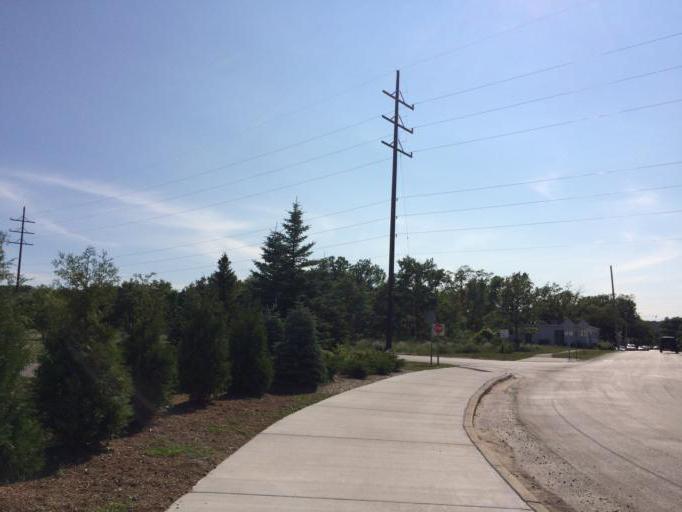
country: US
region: Michigan
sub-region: Grand Traverse County
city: Traverse City
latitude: 44.7517
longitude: -85.6171
